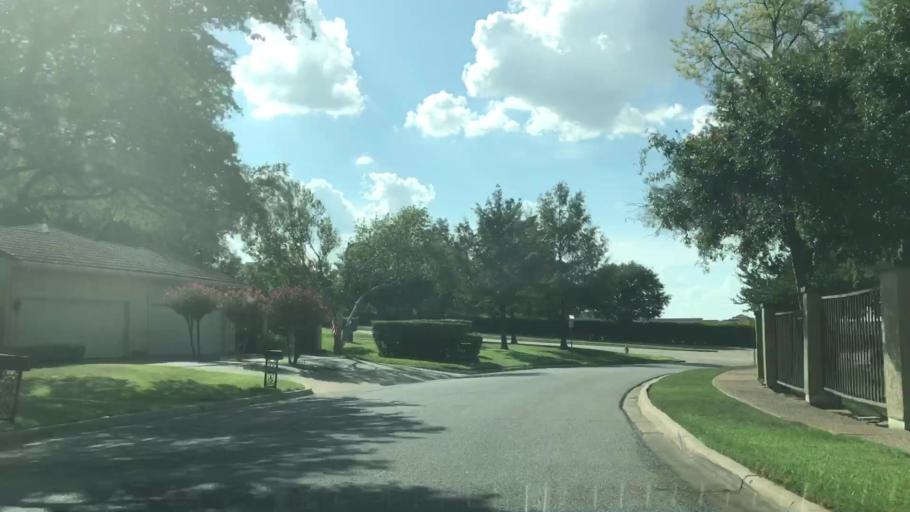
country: US
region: Texas
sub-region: Dallas County
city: Irving
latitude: 32.8590
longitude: -96.9544
